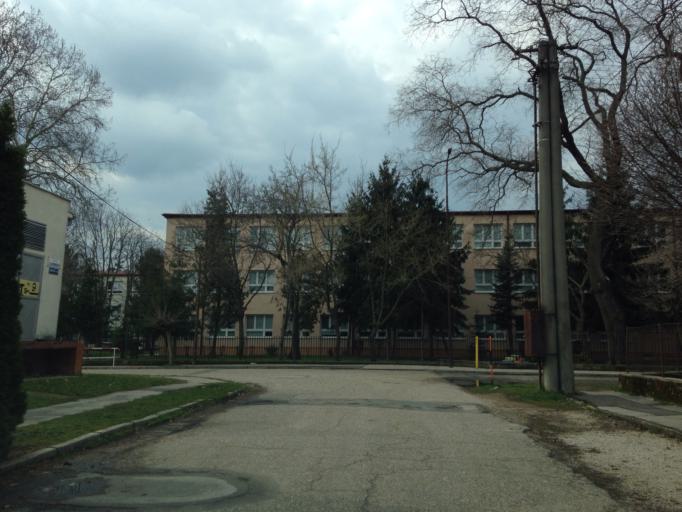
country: SK
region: Nitriansky
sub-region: Okres Nove Zamky
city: Nove Zamky
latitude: 47.9940
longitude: 18.2684
